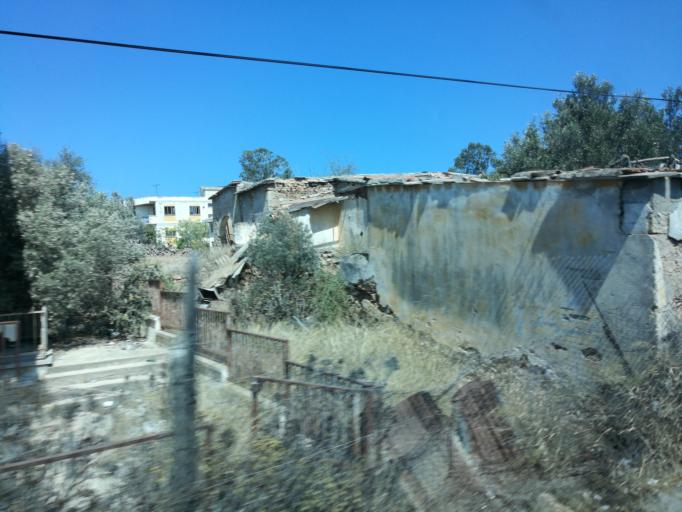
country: CY
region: Ammochostos
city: Famagusta
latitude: 35.1084
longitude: 33.9479
